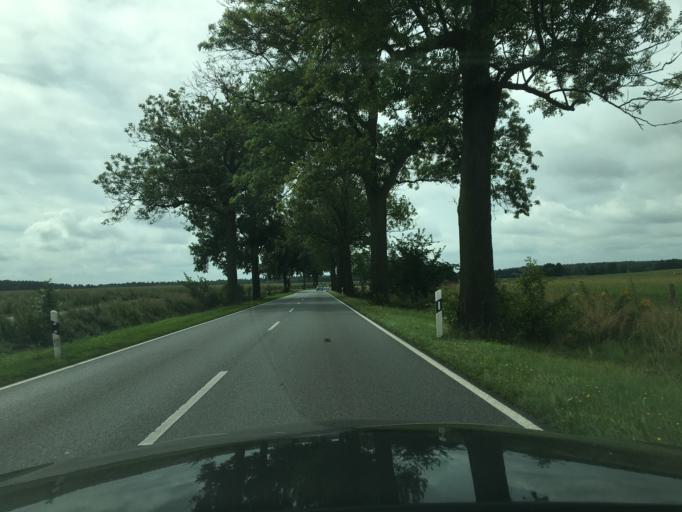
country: DE
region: Brandenburg
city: Gransee
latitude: 52.8837
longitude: 13.1601
